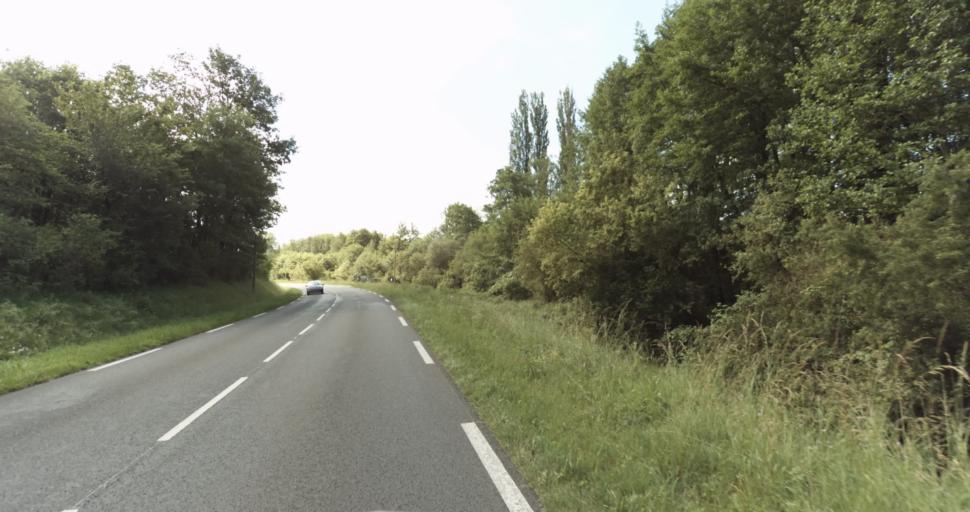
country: FR
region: Aquitaine
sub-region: Departement de la Dordogne
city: Le Bugue
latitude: 44.8434
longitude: 0.8501
